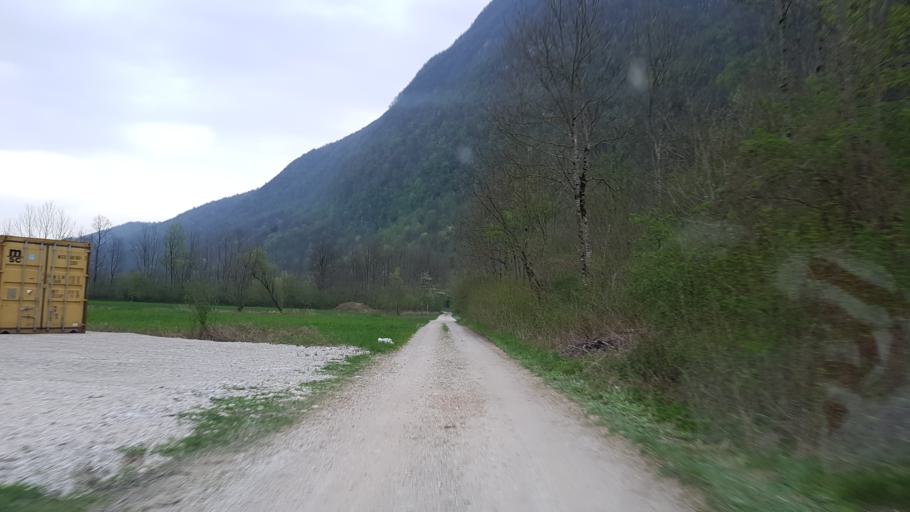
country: SI
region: Kobarid
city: Kobarid
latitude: 46.2442
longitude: 13.5259
